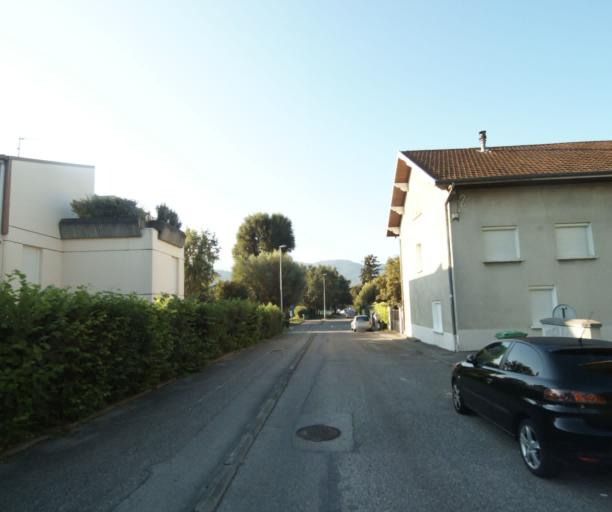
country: FR
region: Rhone-Alpes
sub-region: Departement de l'Isere
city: Corenc
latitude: 45.2082
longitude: 5.7802
